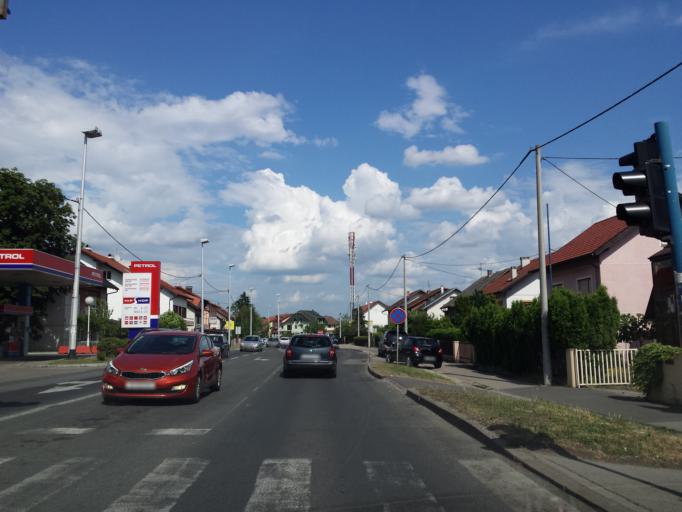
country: HR
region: Grad Zagreb
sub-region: Sesvete
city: Sesvete
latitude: 45.8237
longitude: 16.1311
